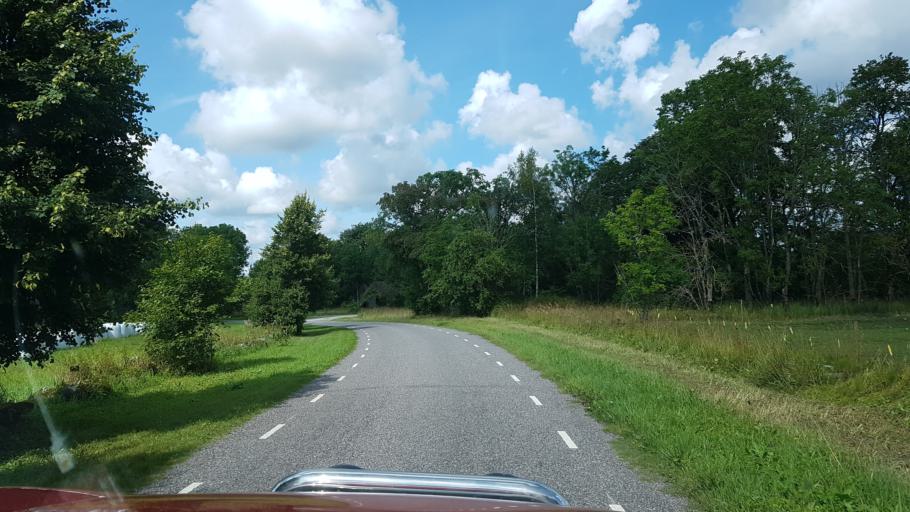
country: EE
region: Raplamaa
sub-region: Rapla vald
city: Rapla
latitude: 58.9676
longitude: 24.6303
